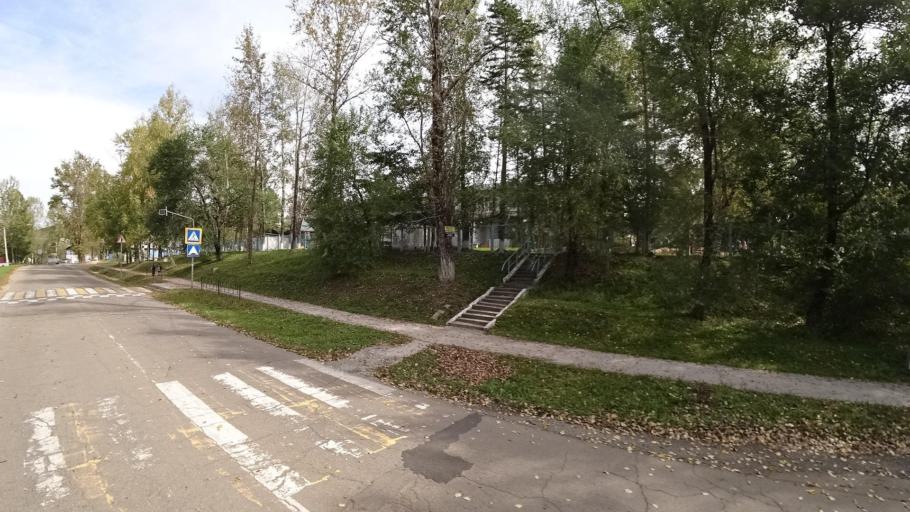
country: RU
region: Jewish Autonomous Oblast
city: Khingansk
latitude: 49.0159
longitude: 131.0596
